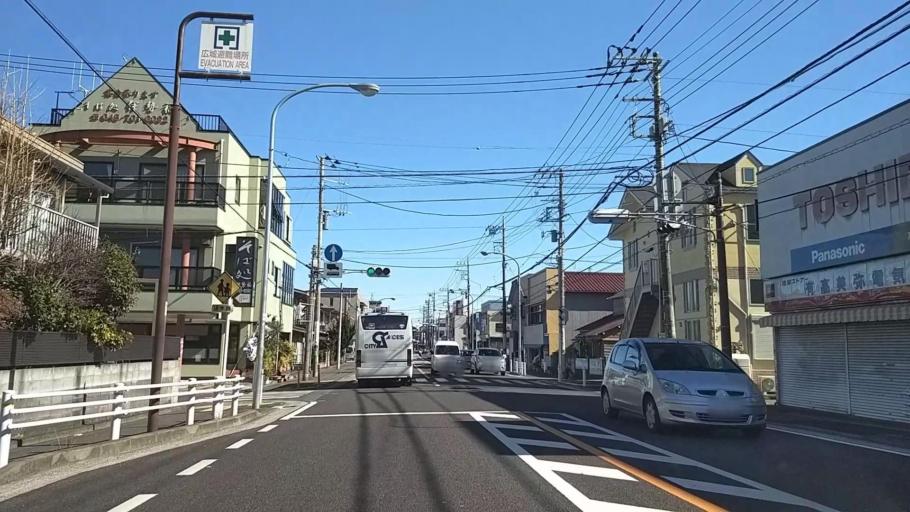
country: JP
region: Kanagawa
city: Zushi
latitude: 35.3289
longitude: 139.6035
